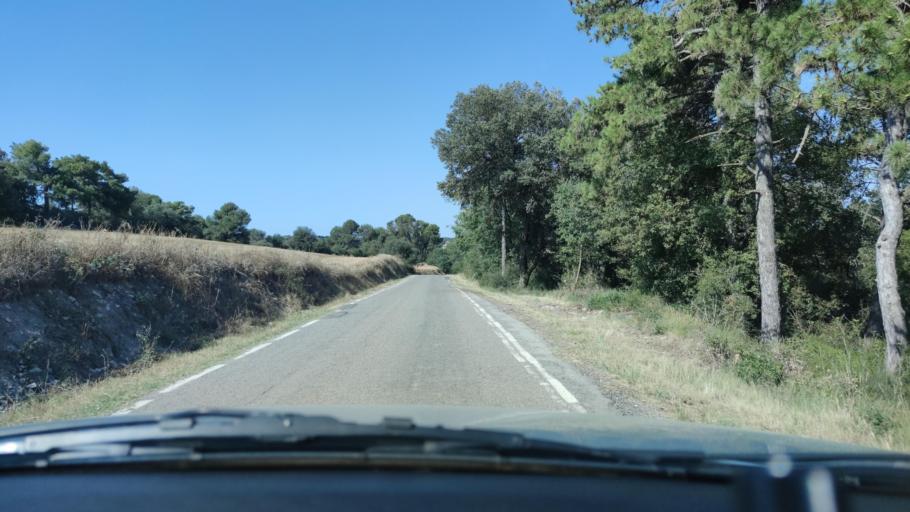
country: ES
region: Catalonia
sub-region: Provincia de Barcelona
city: Pujalt
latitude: 41.6959
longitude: 1.3793
